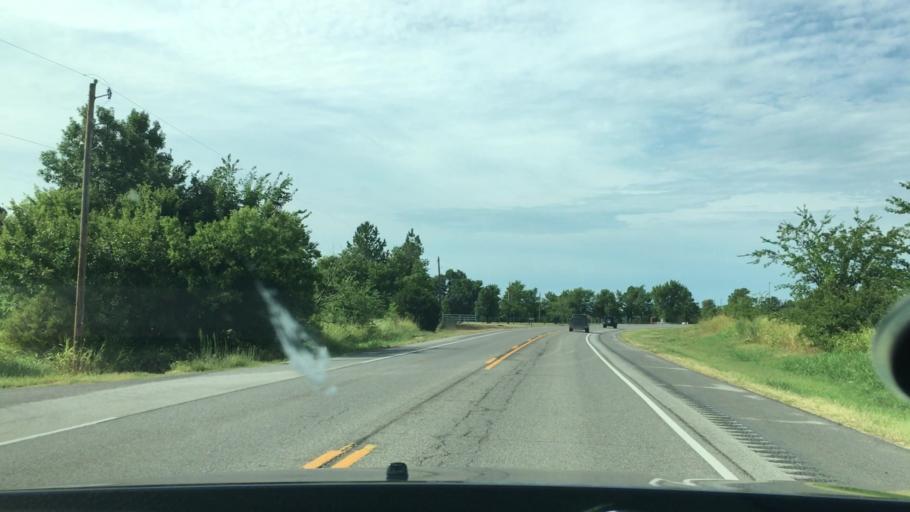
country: US
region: Oklahoma
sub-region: Murray County
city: Sulphur
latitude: 34.5328
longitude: -96.9674
